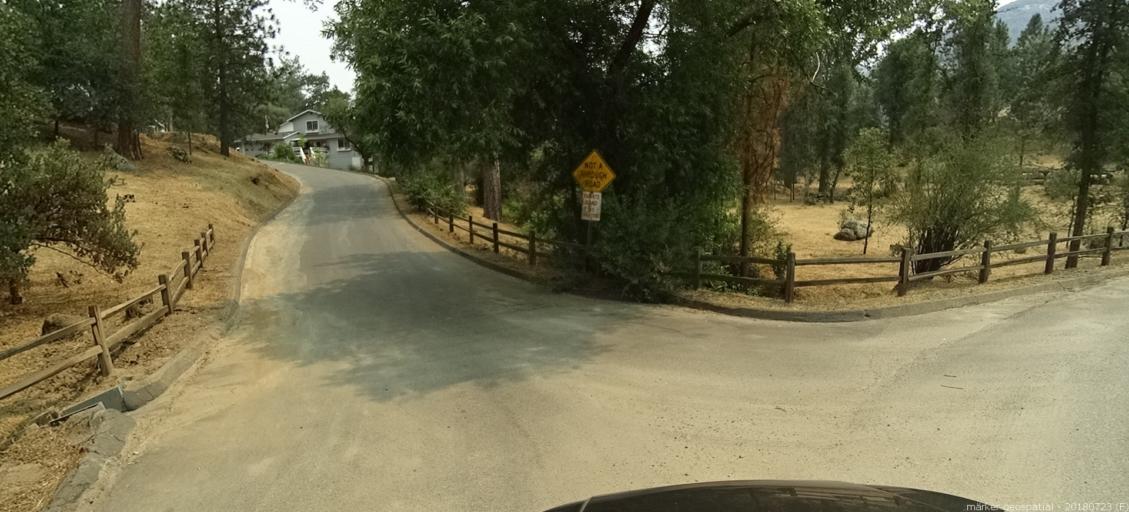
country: US
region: California
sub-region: Madera County
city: Oakhurst
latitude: 37.3276
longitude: -119.6652
